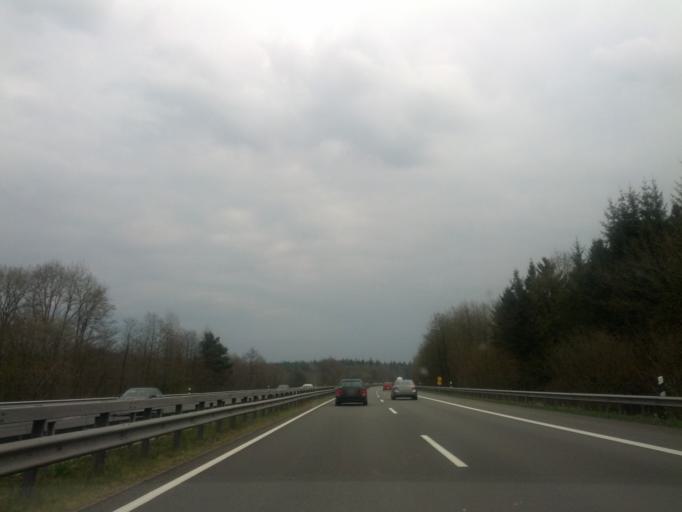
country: DE
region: Lower Saxony
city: Bad Zwischenahn
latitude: 53.2455
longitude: 8.0141
